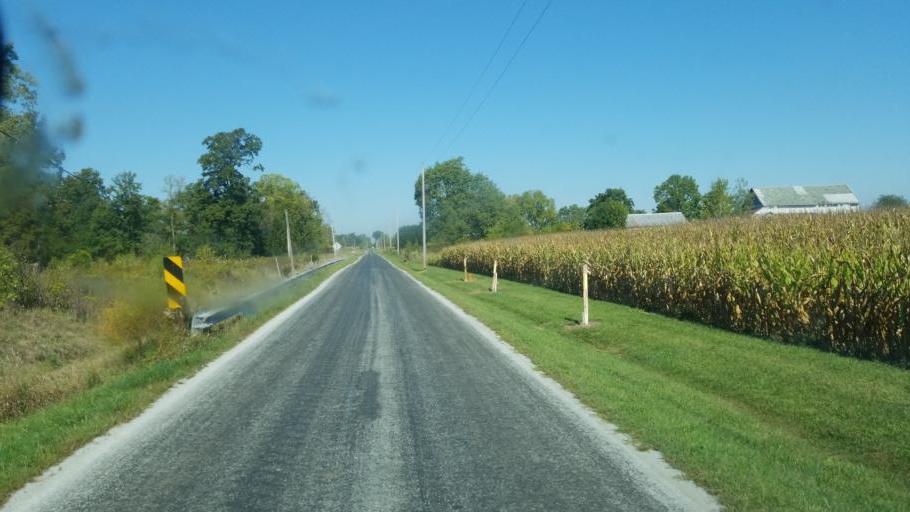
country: US
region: Ohio
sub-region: Hardin County
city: Kenton
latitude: 40.5884
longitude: -83.4746
